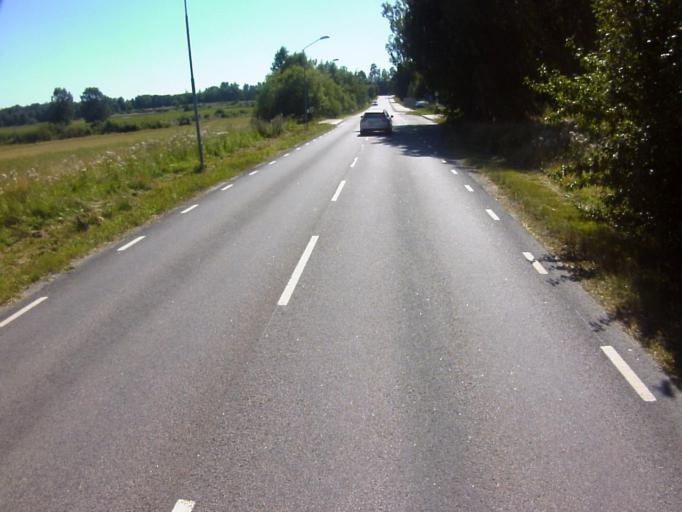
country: SE
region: Soedermanland
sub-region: Eskilstuna Kommun
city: Hallbybrunn
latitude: 59.3839
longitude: 16.4354
